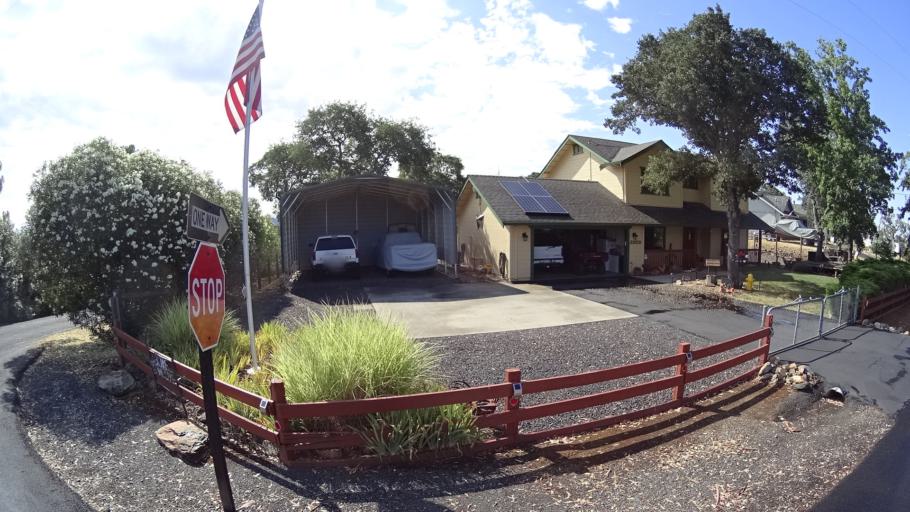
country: US
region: California
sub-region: Calaveras County
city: Copperopolis
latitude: 37.9104
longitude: -120.6125
